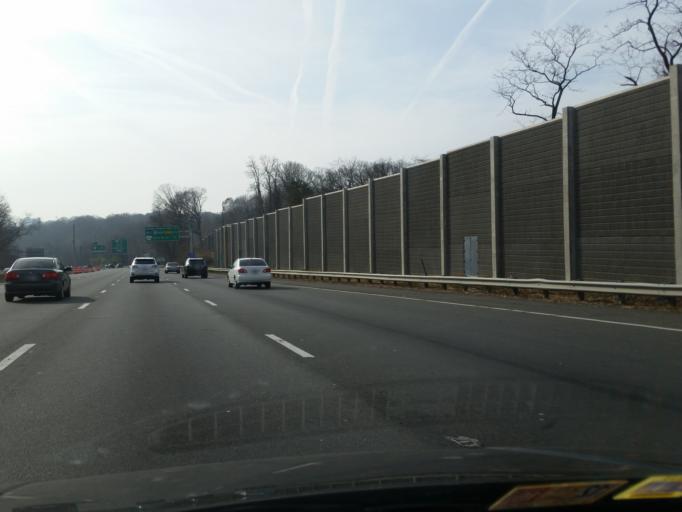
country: US
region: Virginia
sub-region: Fairfax County
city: McLean
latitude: 38.9503
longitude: -77.1982
